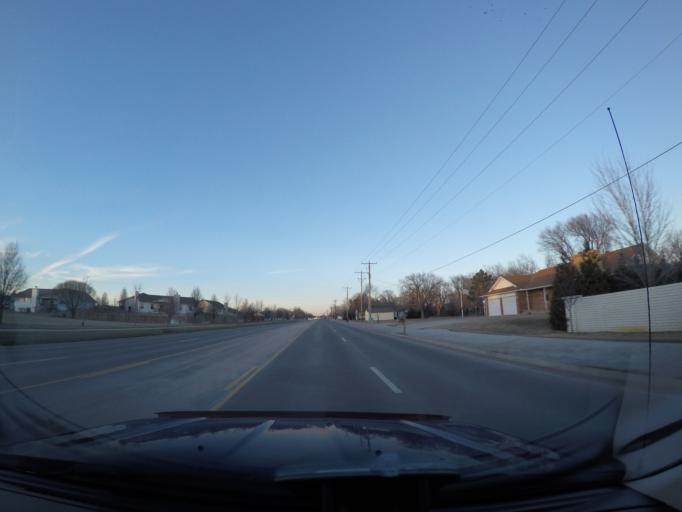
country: US
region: Kansas
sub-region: Sedgwick County
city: Goddard
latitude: 37.6541
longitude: -97.4807
